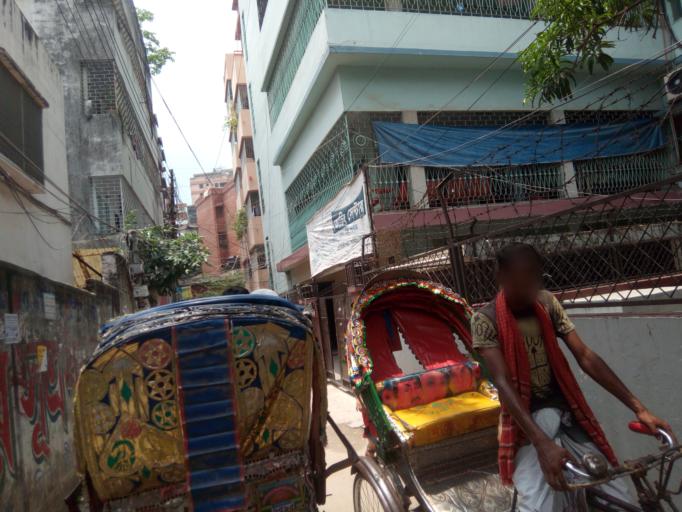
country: BD
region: Dhaka
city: Paltan
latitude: 23.7454
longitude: 90.4088
